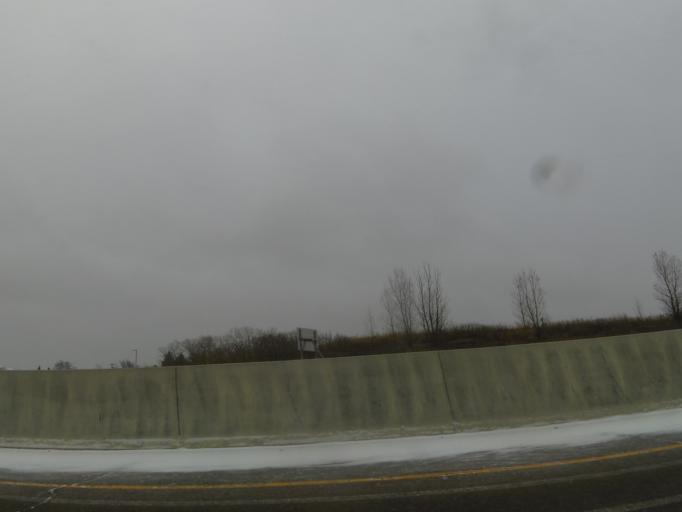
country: US
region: Minnesota
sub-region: Dakota County
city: Eagan
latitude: 44.8110
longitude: -93.2195
